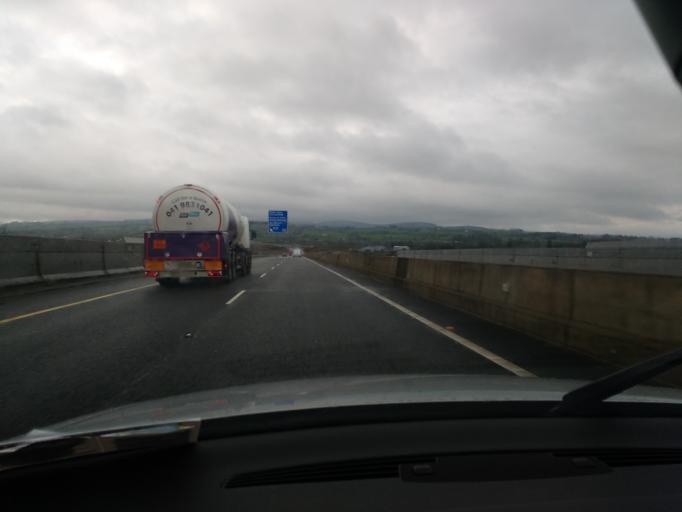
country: IE
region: Munster
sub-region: North Tipperary
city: Nenagh
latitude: 52.8446
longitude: -8.2345
